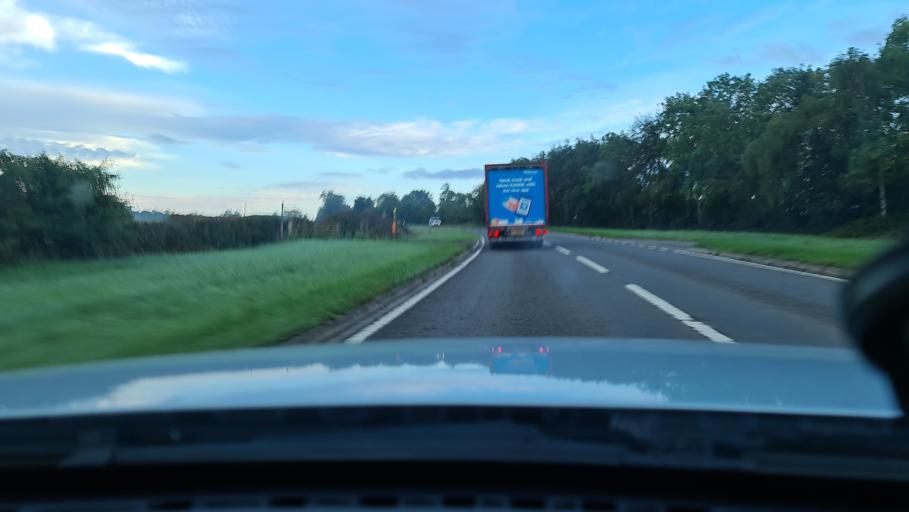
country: GB
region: England
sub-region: Warwickshire
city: Southam
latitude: 52.2198
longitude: -1.3889
